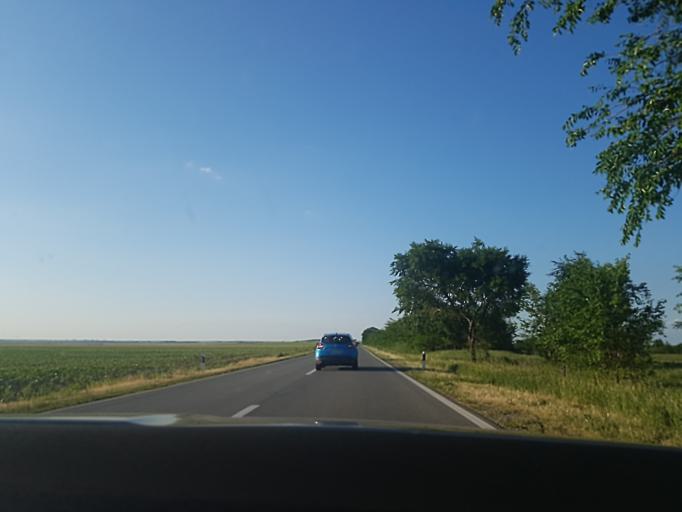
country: RS
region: Autonomna Pokrajina Vojvodina
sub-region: Juznobanatski Okrug
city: Vrsac
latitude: 45.1815
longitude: 21.2960
